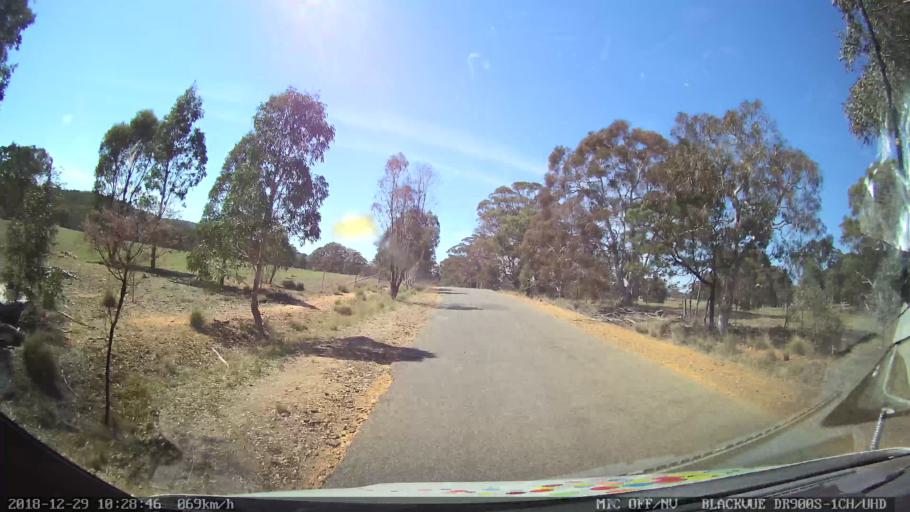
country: AU
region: New South Wales
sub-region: Yass Valley
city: Gundaroo
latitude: -34.9456
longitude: 149.4553
